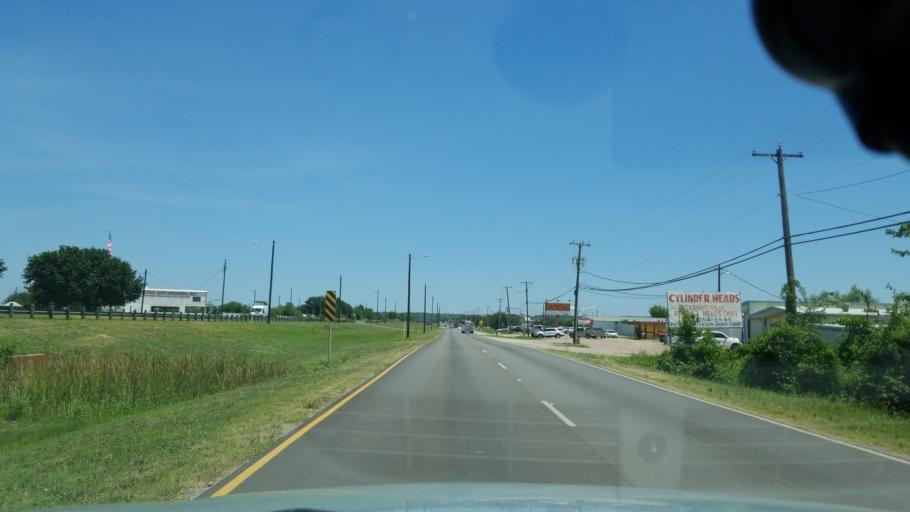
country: US
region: Texas
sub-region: Dallas County
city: Grand Prairie
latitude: 32.7463
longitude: -96.9501
